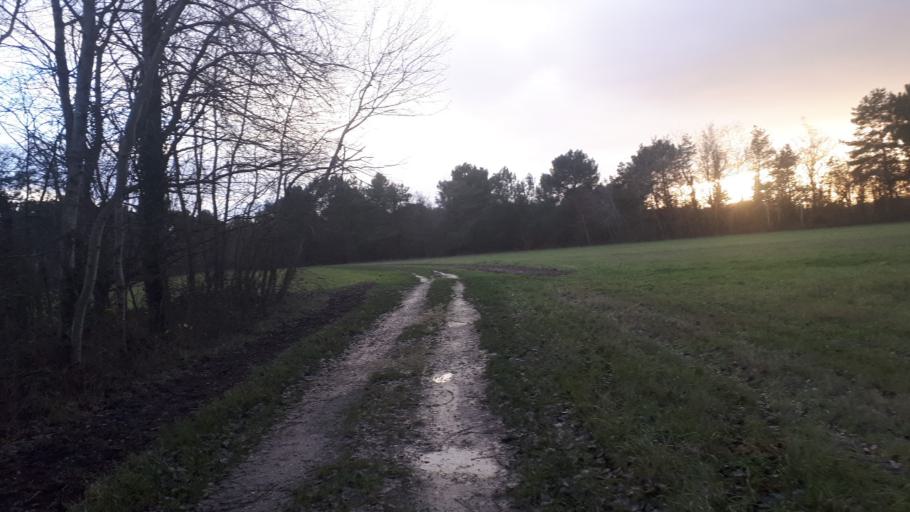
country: FR
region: Centre
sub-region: Departement du Loir-et-Cher
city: Saint-Romain-sur-Cher
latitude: 47.3469
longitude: 1.3955
